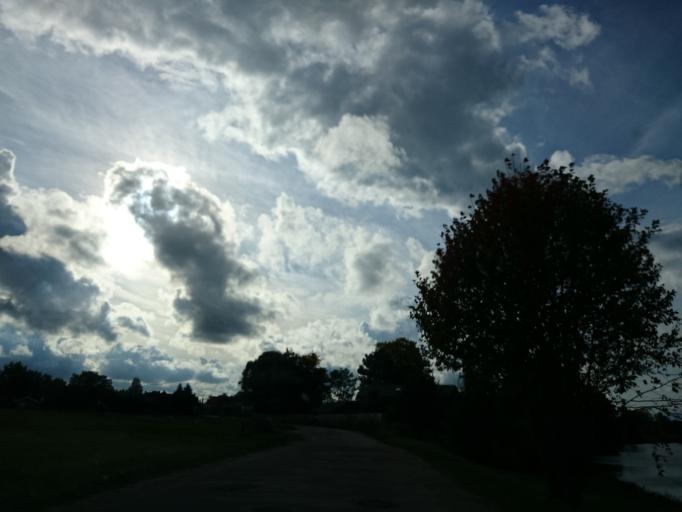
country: LV
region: Adazi
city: Adazi
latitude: 57.0714
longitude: 24.3397
